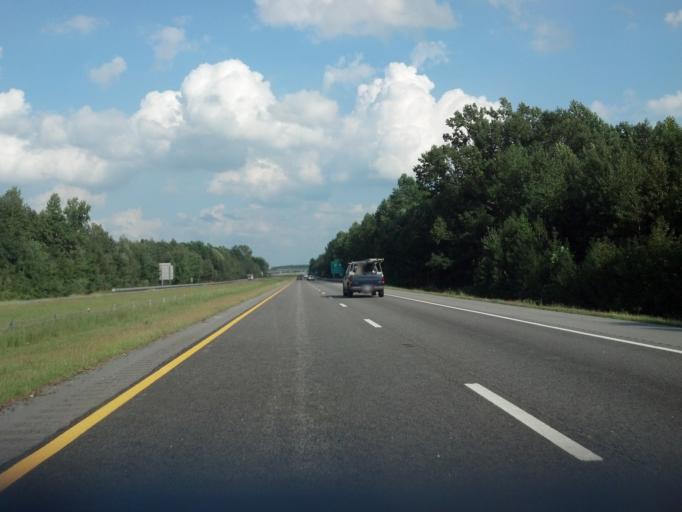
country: US
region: North Carolina
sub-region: Pitt County
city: Bethel
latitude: 35.8388
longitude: -77.3909
